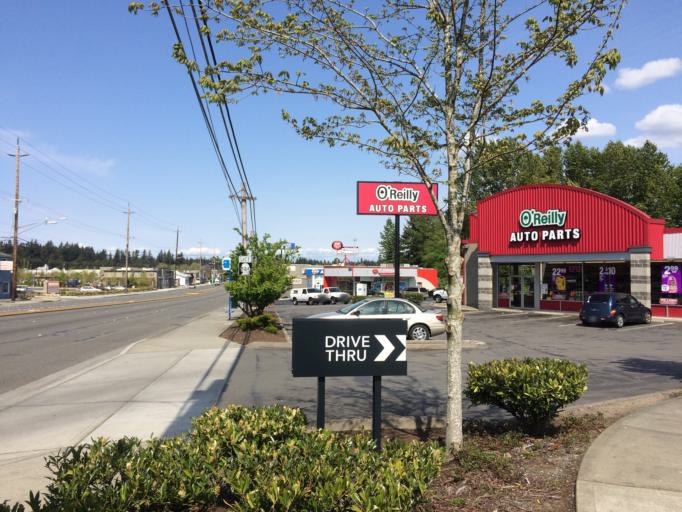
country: US
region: Washington
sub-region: Snohomish County
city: Lynnwood
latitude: 47.8179
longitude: -122.3177
